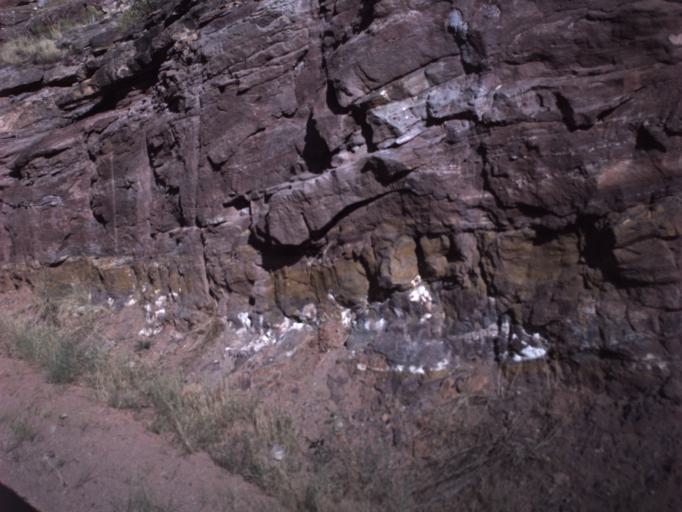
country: US
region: Utah
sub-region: Grand County
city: Moab
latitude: 38.6772
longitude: -109.4870
